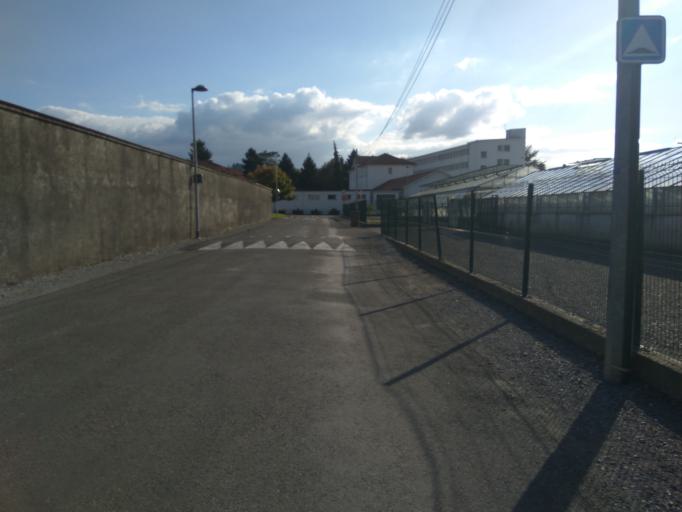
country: FR
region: Aquitaine
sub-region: Departement des Pyrenees-Atlantiques
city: Gelos
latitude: 43.2859
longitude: -0.3710
